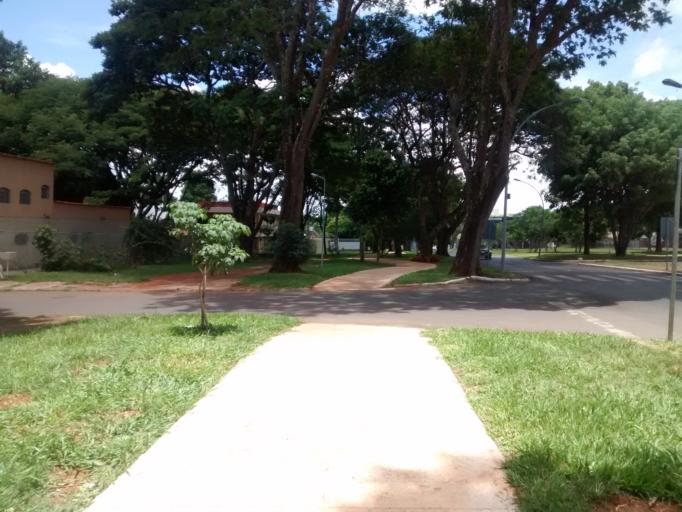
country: BR
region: Federal District
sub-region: Brasilia
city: Brasilia
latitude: -15.8101
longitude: -47.9075
